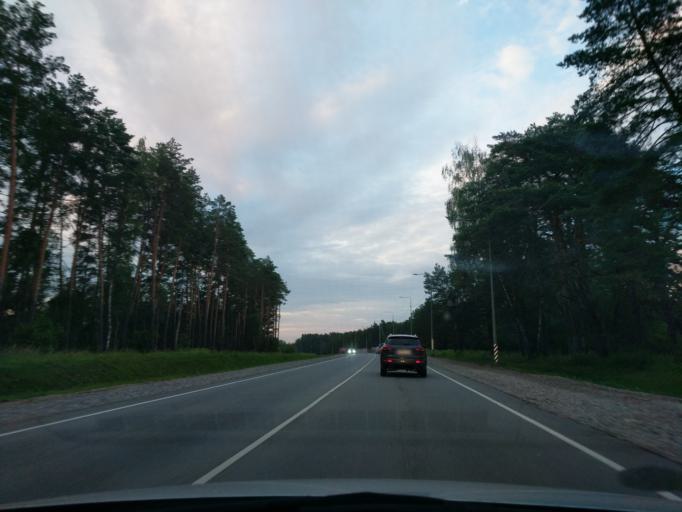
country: RU
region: Kaluga
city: Maloyaroslavets
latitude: 55.0407
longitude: 36.5455
